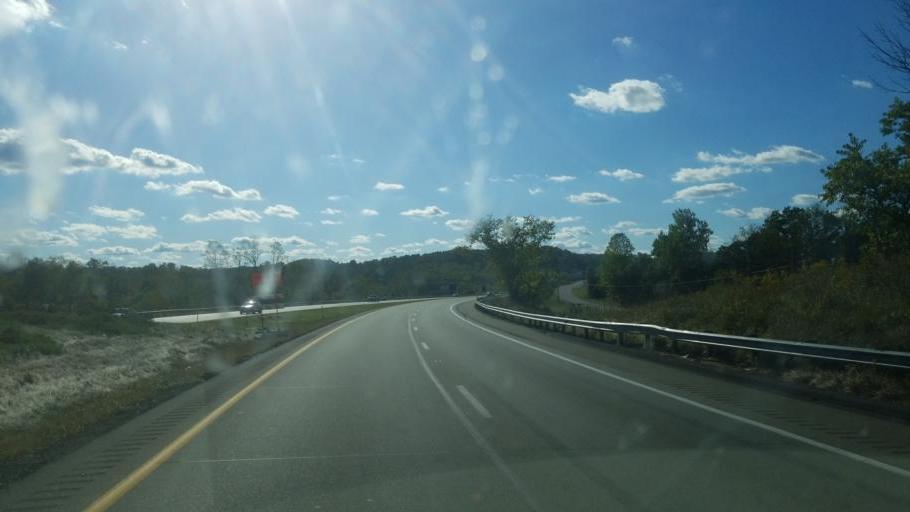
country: US
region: Pennsylvania
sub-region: Washington County
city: Wolfdale
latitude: 40.1309
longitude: -80.3265
